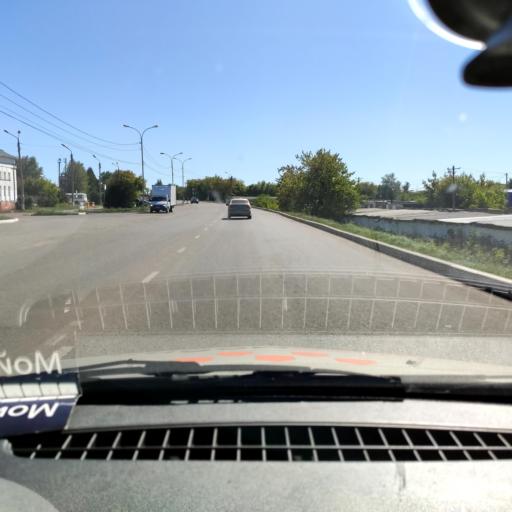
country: RU
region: Bashkortostan
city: Kumertau
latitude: 52.7596
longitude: 55.8096
